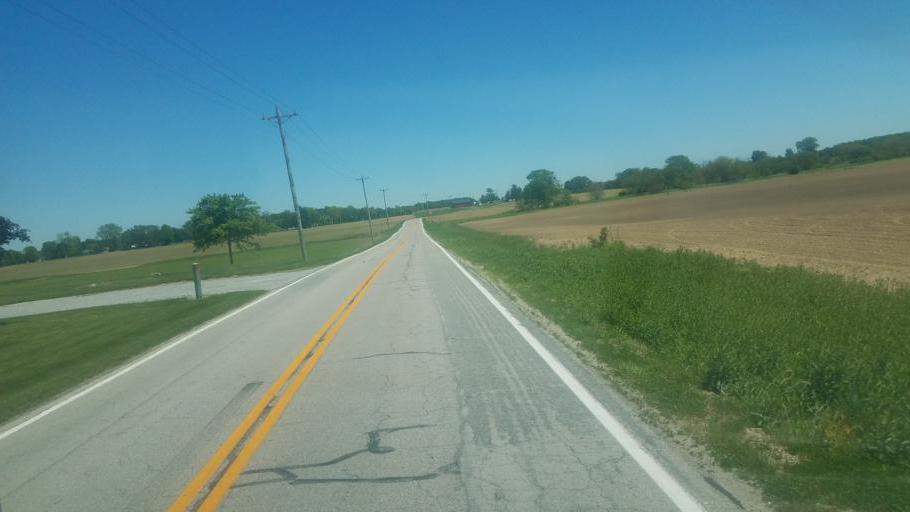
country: US
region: Ohio
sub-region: Miami County
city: Piqua
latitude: 40.2130
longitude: -84.2969
